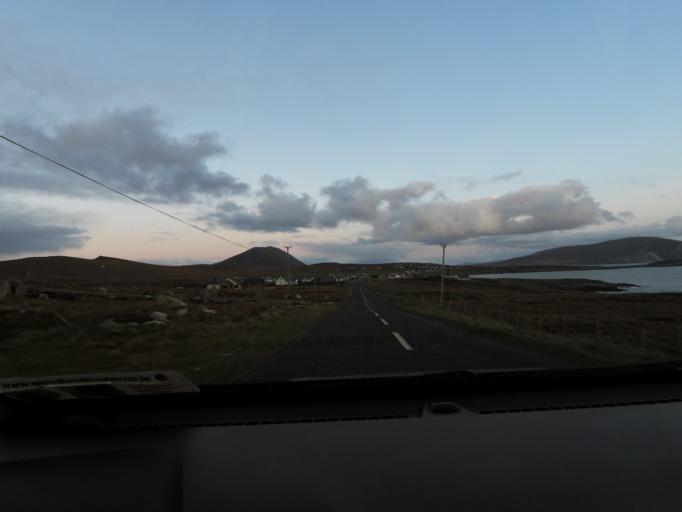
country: IE
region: Connaught
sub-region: Maigh Eo
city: Belmullet
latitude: 53.9701
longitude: -10.1504
